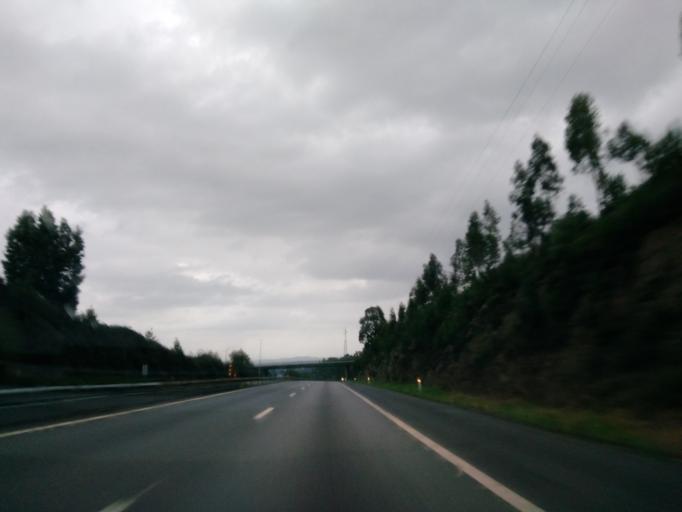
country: PT
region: Porto
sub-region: Santo Tirso
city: Santo Tirso
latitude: 41.3406
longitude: -8.5071
